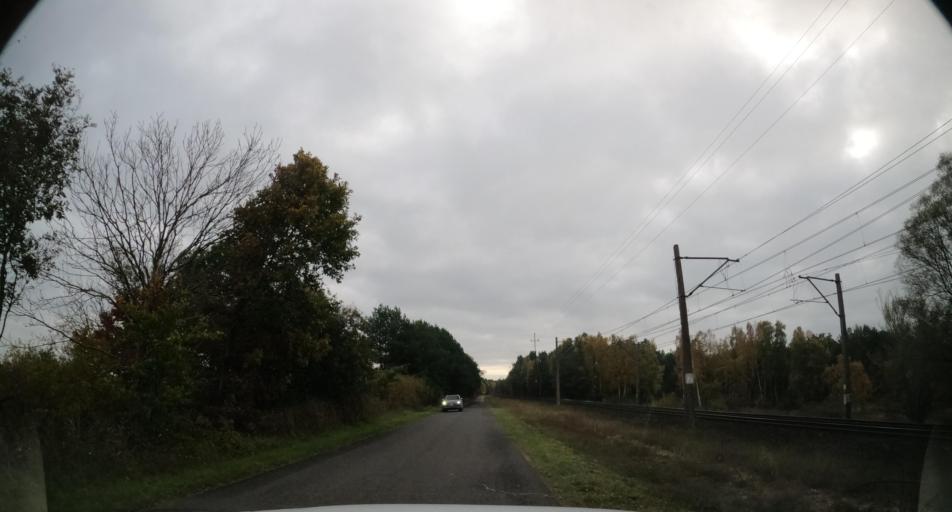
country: PL
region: West Pomeranian Voivodeship
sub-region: Powiat kamienski
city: Miedzyzdroje
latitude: 53.9234
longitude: 14.5527
